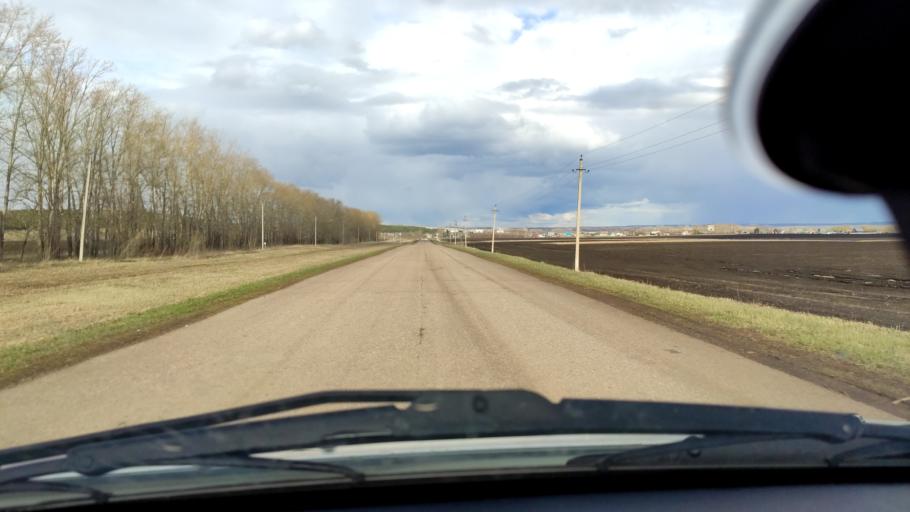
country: RU
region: Bashkortostan
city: Buzdyak
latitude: 54.7639
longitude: 54.5832
